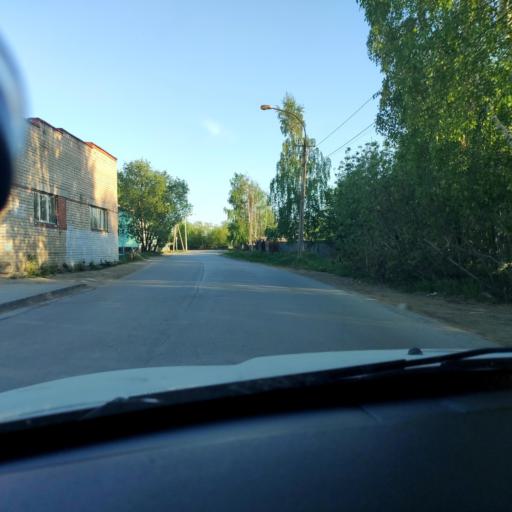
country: RU
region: Perm
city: Polazna
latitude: 58.1458
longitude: 56.4475
